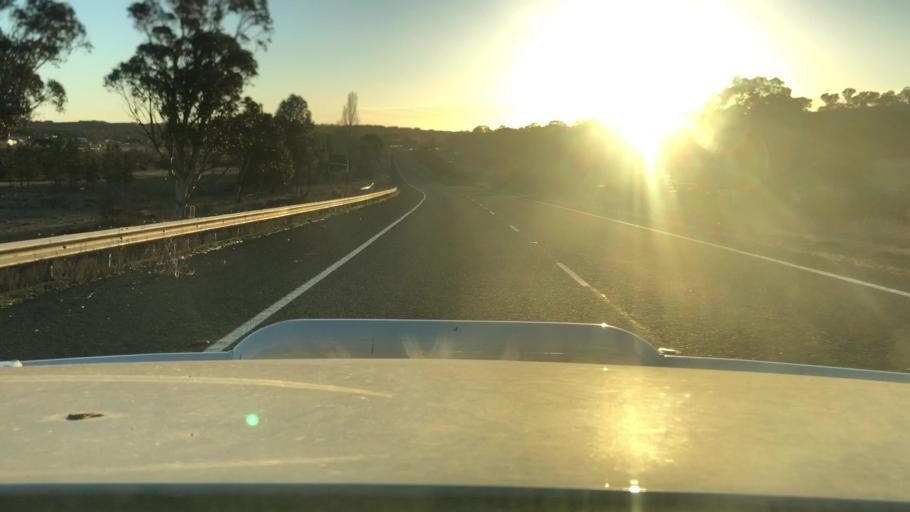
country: AU
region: New South Wales
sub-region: Goulburn Mulwaree
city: Goulburn
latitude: -34.7858
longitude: 149.6581
